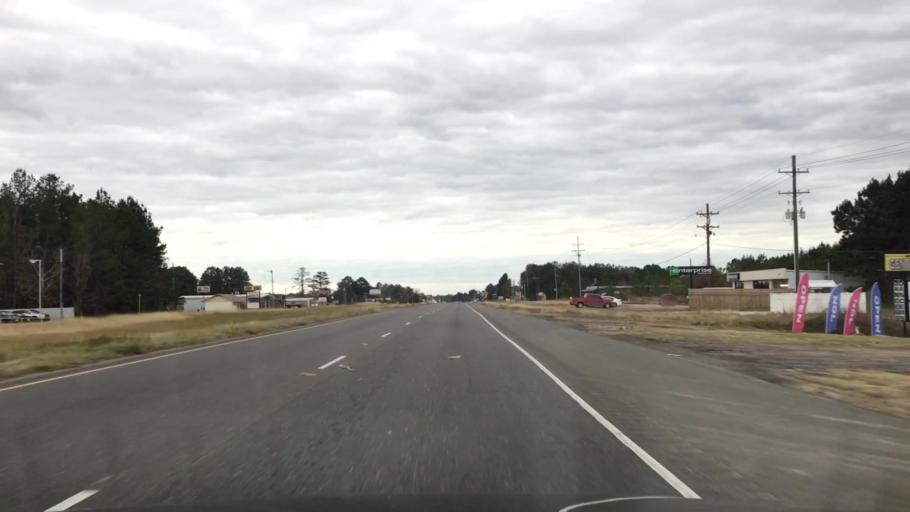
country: US
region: Louisiana
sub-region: Vernon Parish
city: New Llano
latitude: 31.0879
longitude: -93.2715
